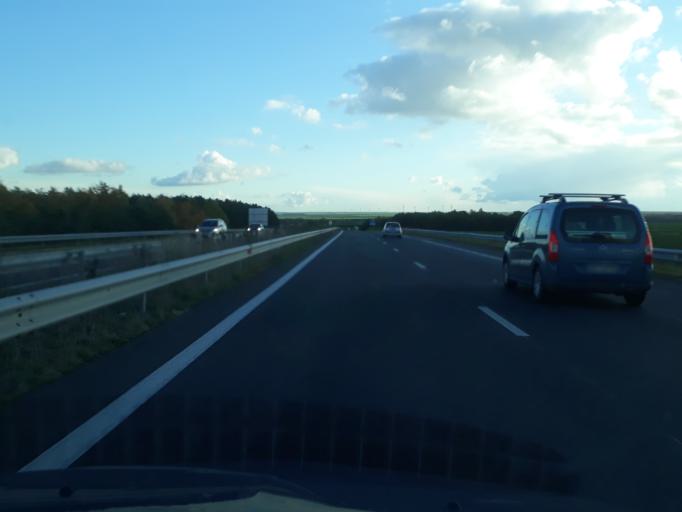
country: FR
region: Champagne-Ardenne
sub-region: Departement de la Marne
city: Fagnieres
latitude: 48.8956
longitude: 4.2868
